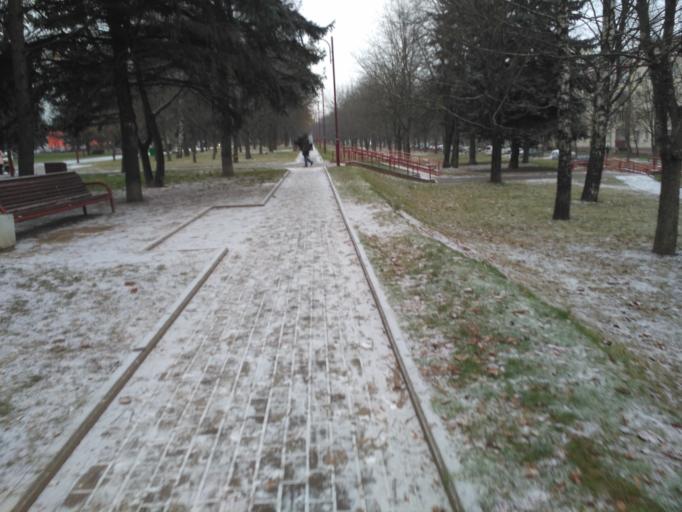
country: BY
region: Minsk
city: Novoye Medvezhino
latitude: 53.9115
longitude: 27.4880
